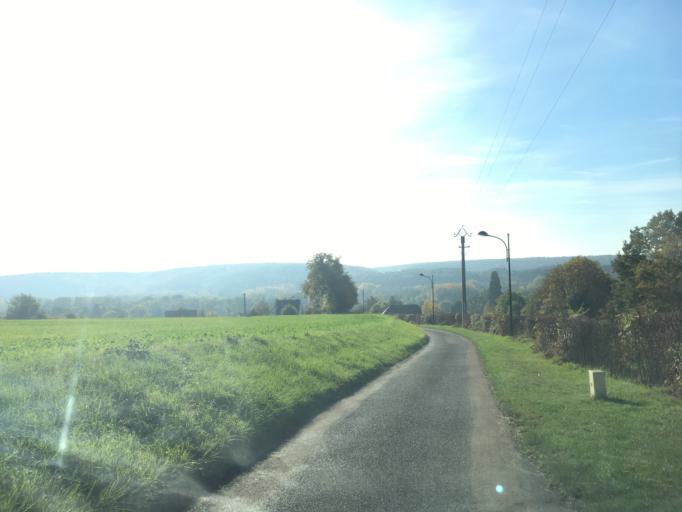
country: FR
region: Haute-Normandie
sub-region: Departement de l'Eure
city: Heudreville-sur-Eure
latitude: 49.1337
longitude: 1.2157
